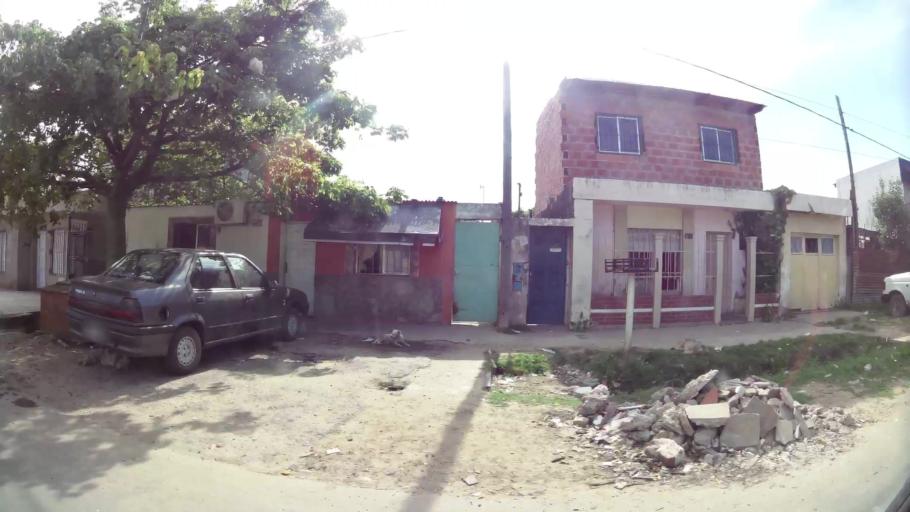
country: AR
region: Santa Fe
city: Granadero Baigorria
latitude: -32.9146
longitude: -60.7177
